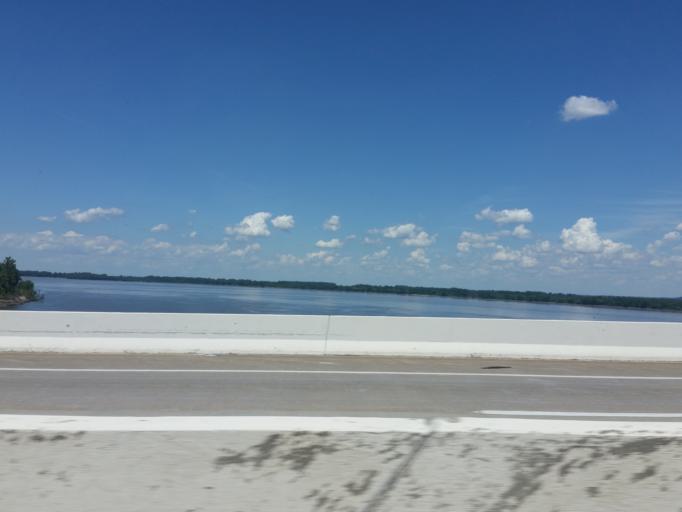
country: US
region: Missouri
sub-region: Pemiscot County
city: Caruthersville
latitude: 36.1179
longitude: -89.6147
